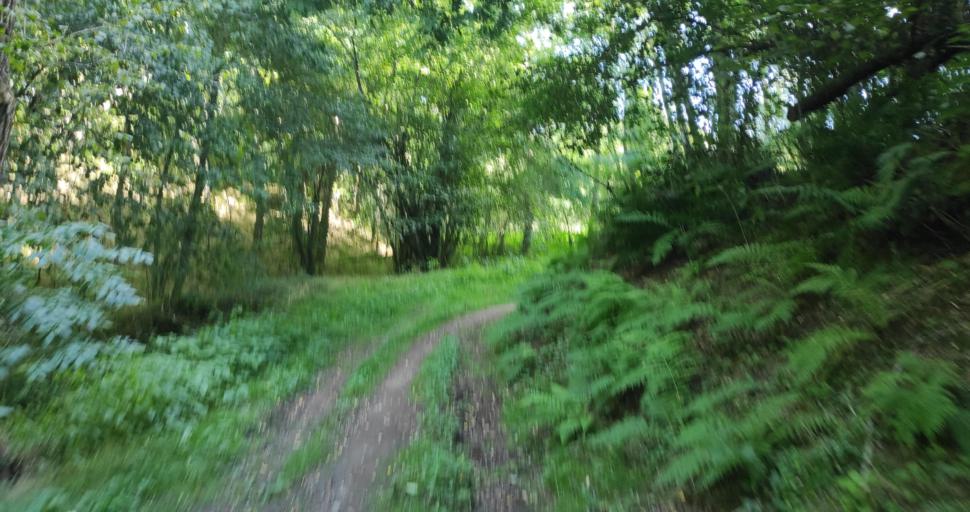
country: FR
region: Midi-Pyrenees
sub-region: Departement de l'Aveyron
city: Cransac
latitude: 44.5343
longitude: 2.2746
